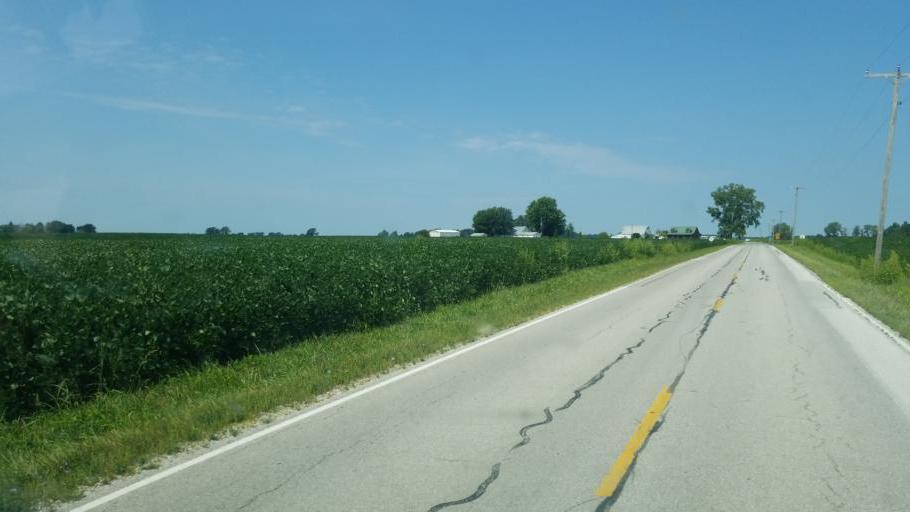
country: US
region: Ohio
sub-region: Marion County
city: Marion
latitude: 40.6699
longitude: -83.2303
